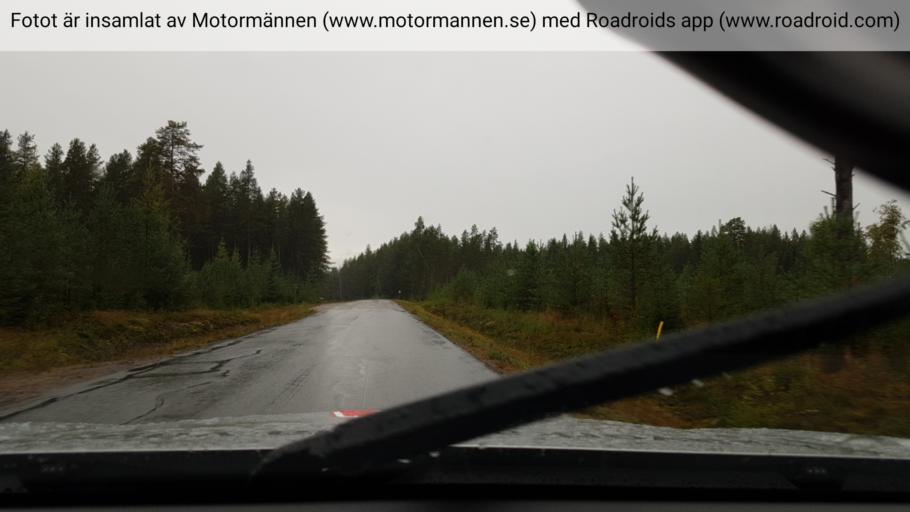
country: SE
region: Vaesterbotten
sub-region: Skelleftea Kommun
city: Burea
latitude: 64.3799
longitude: 21.1226
